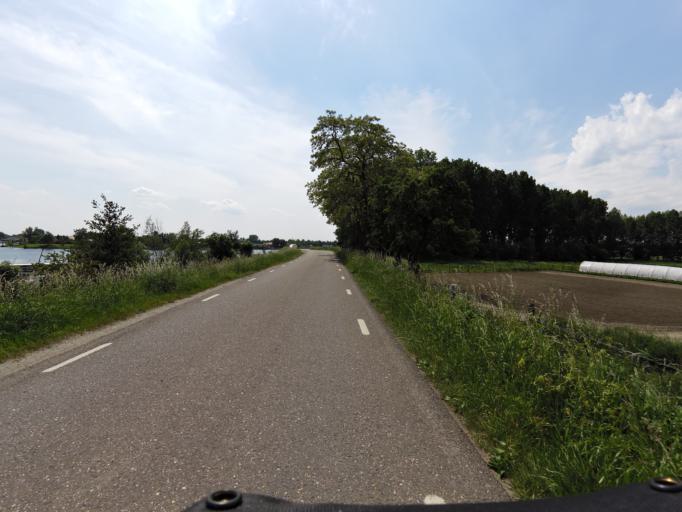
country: NL
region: North Brabant
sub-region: Gemeente Aalburg
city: Aalburg
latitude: 51.7878
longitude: 5.0885
